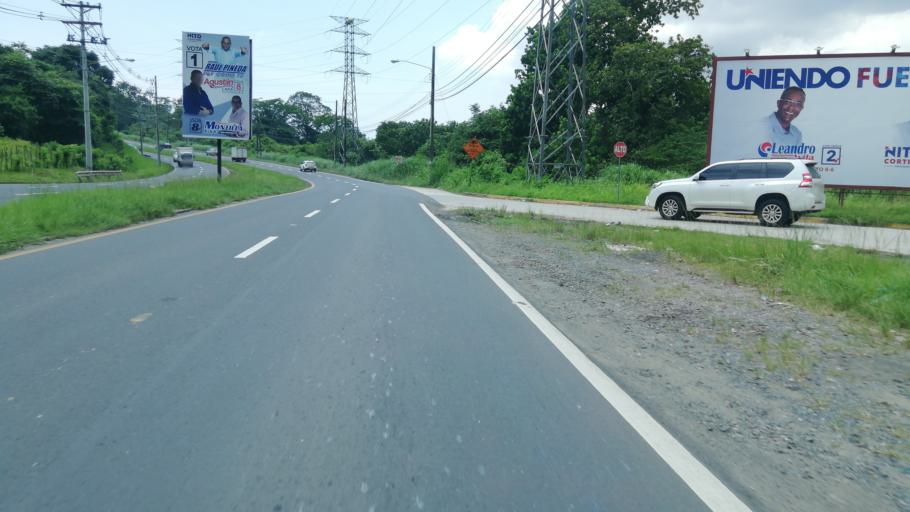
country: PA
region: Panama
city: San Miguelito
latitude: 9.0684
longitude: -79.4626
